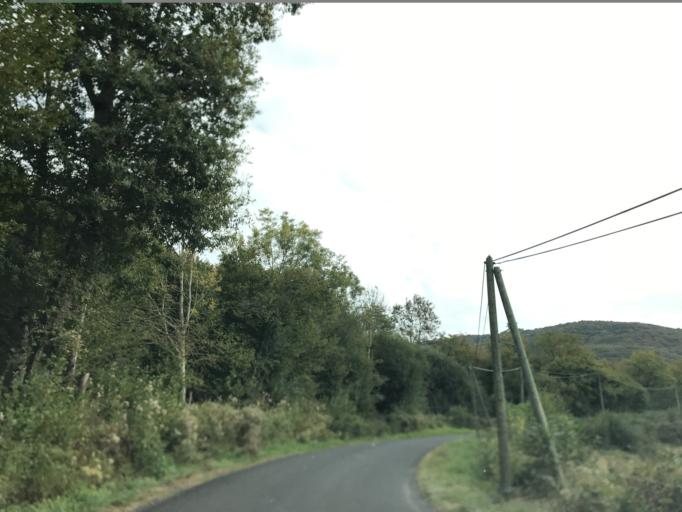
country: FR
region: Auvergne
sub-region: Departement du Puy-de-Dome
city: Celles-sur-Durolle
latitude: 45.8253
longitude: 3.6262
